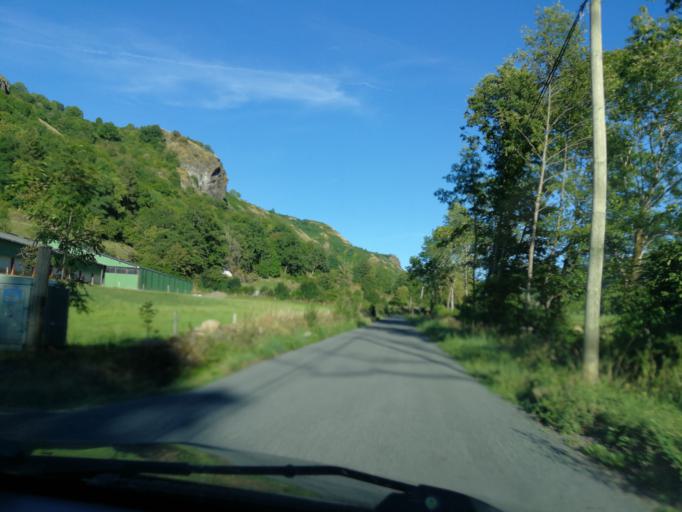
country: FR
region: Auvergne
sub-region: Departement du Cantal
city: Saint-Cernin
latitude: 45.1081
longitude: 2.5146
